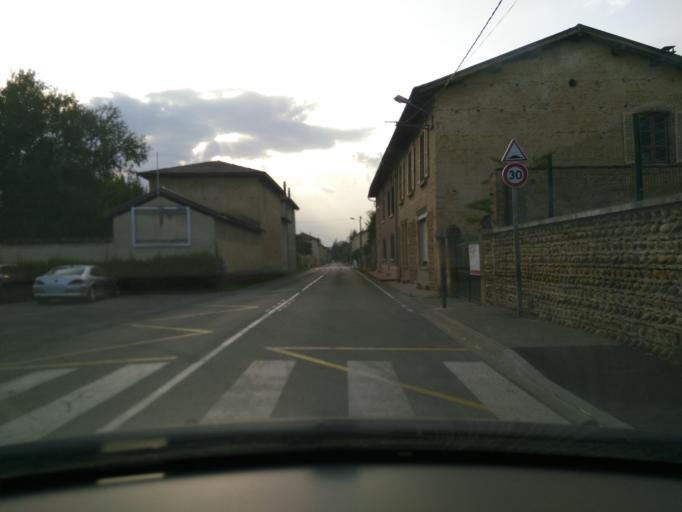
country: FR
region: Rhone-Alpes
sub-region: Departement de l'Isere
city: Viriville
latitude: 45.3934
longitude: 5.1662
